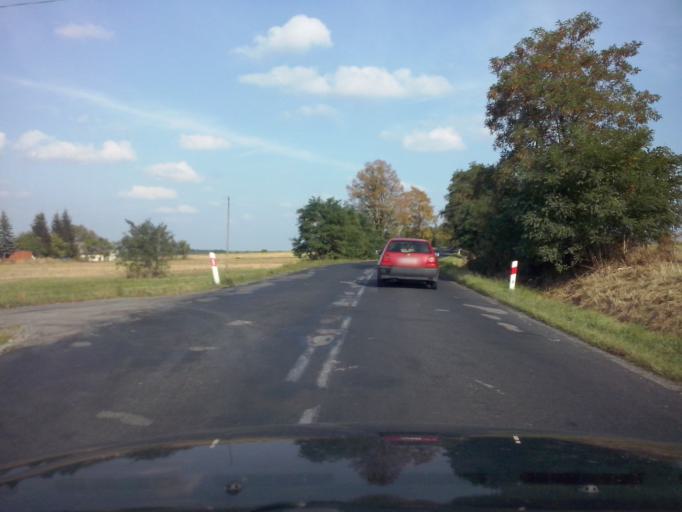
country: PL
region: Subcarpathian Voivodeship
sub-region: Powiat kolbuszowski
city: Dzikowiec
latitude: 50.2592
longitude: 21.8359
